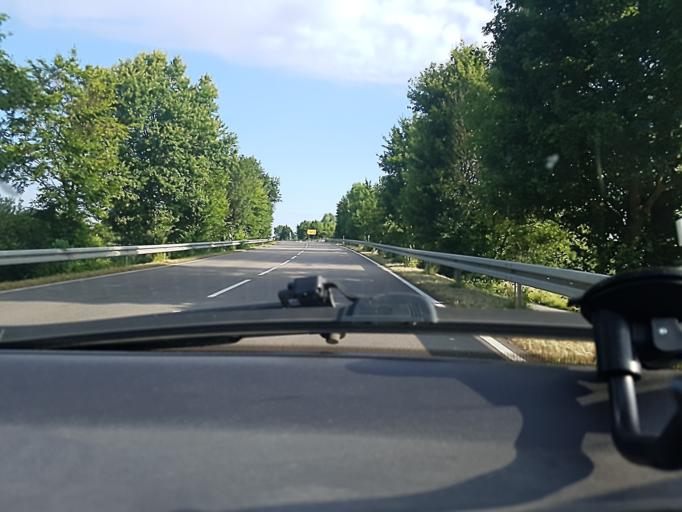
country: DE
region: Baden-Wuerttemberg
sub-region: Freiburg Region
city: Willstatt
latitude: 48.5320
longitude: 7.9242
